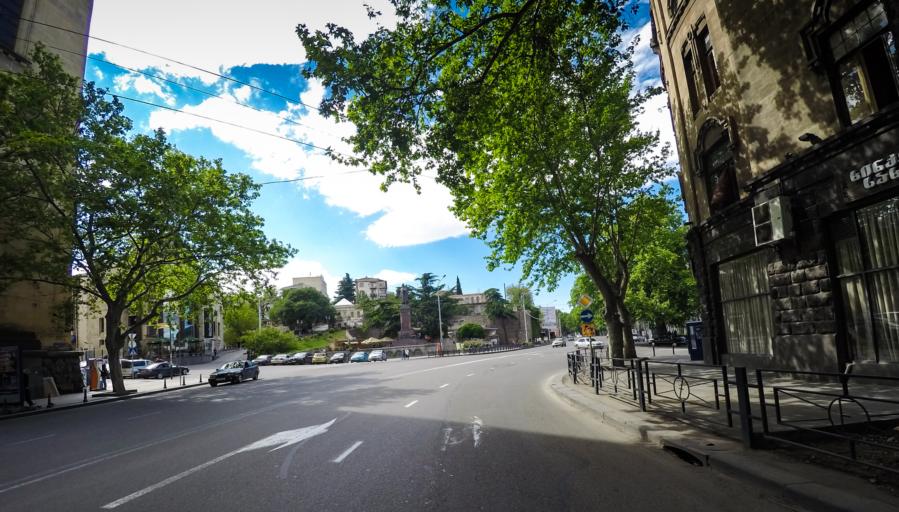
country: GE
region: T'bilisi
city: Tbilisi
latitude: 41.7035
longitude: 44.7907
